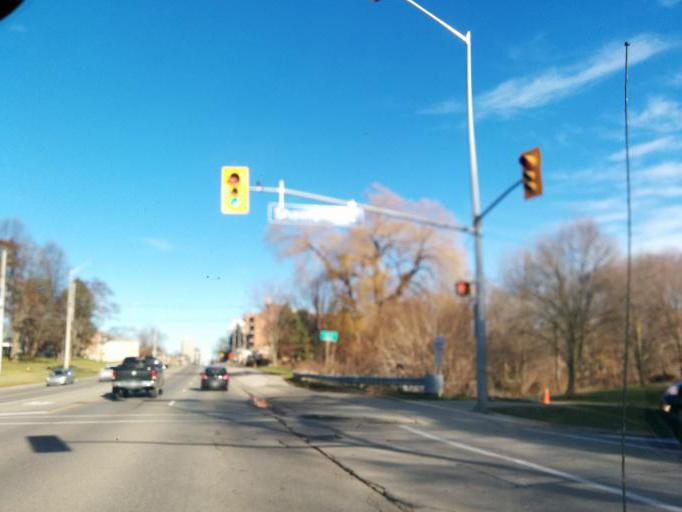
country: CA
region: Ontario
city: Mississauga
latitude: 43.5404
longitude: -79.5980
